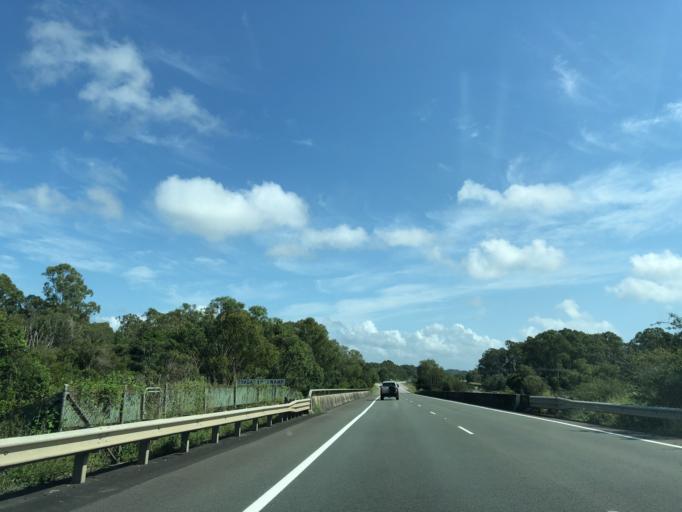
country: AU
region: New South Wales
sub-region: Byron Shire
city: Brunswick Heads
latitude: -28.6024
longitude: 153.5455
